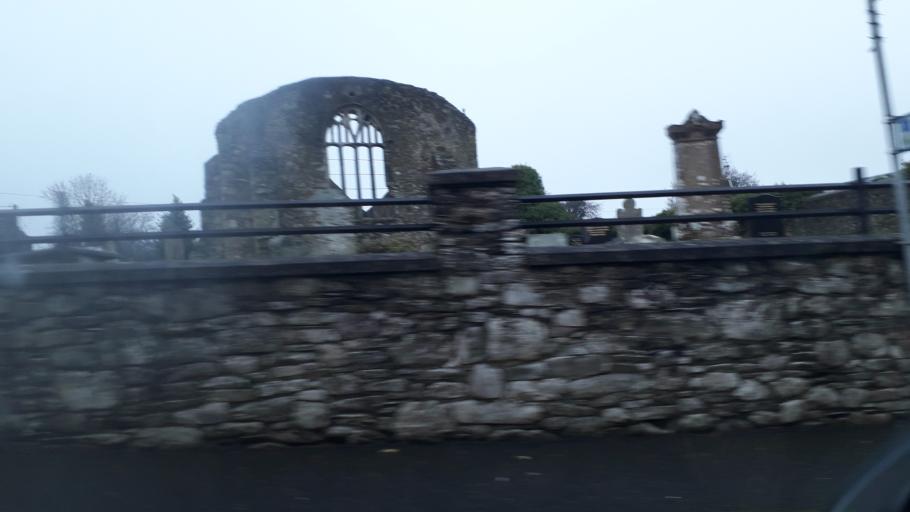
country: IE
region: Ulster
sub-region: County Donegal
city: Ramelton
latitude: 55.0360
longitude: -7.6454
